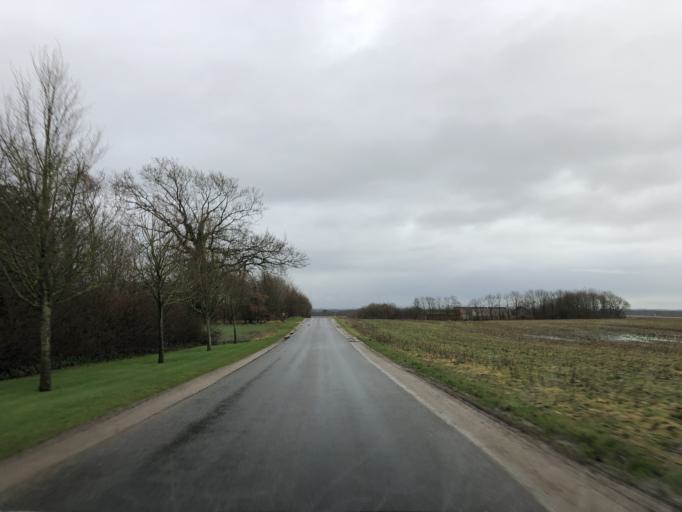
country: DK
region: Central Jutland
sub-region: Holstebro Kommune
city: Holstebro
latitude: 56.3761
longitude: 8.7281
